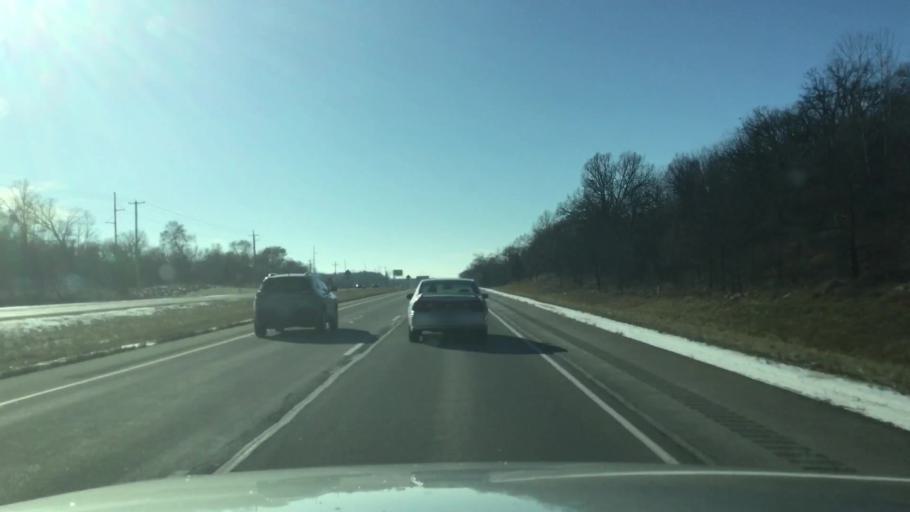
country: US
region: Wisconsin
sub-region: Racine County
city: Browns Lake
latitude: 42.7140
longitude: -88.2311
